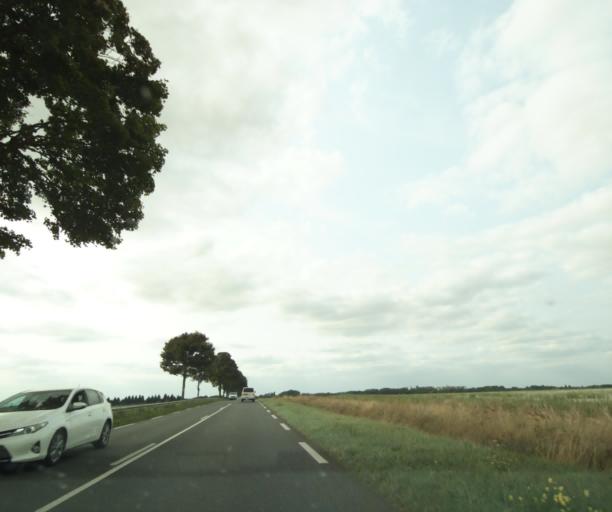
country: FR
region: Centre
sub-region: Departement d'Indre-et-Loire
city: Reignac-sur-Indre
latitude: 47.2017
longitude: 0.9118
